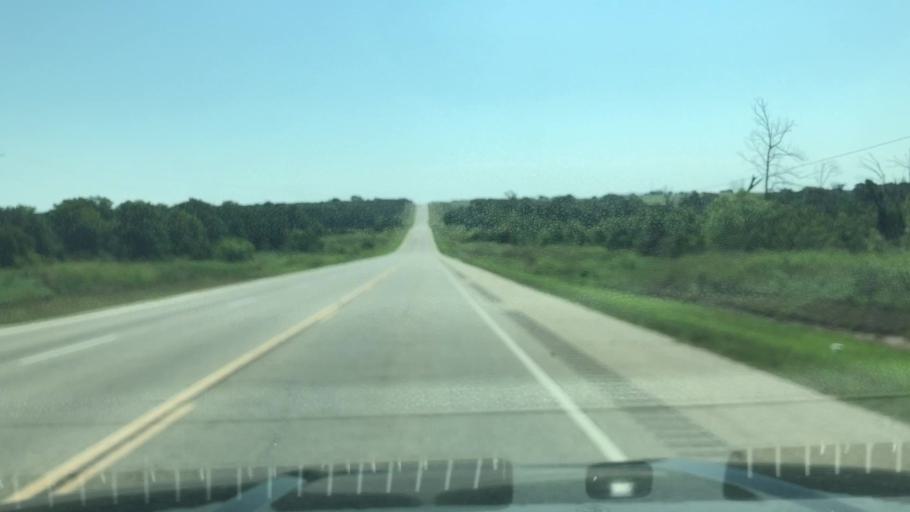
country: US
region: Oklahoma
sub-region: Creek County
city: Mannford
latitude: 36.0030
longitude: -96.4312
